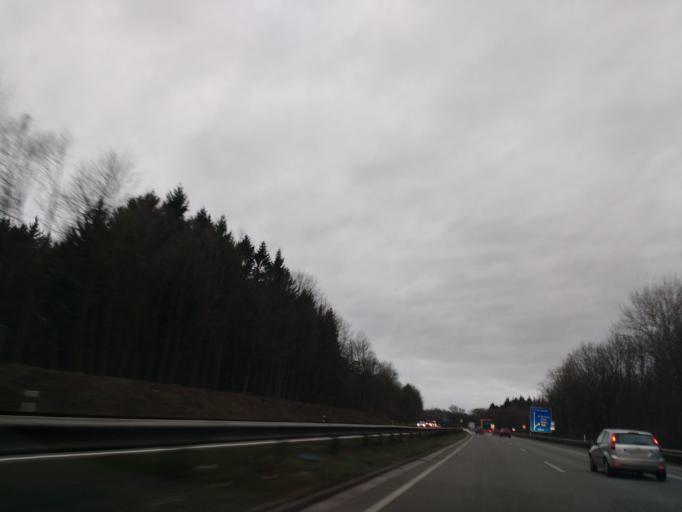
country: DE
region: Lower Saxony
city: Seevetal
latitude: 53.4186
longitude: 9.9253
